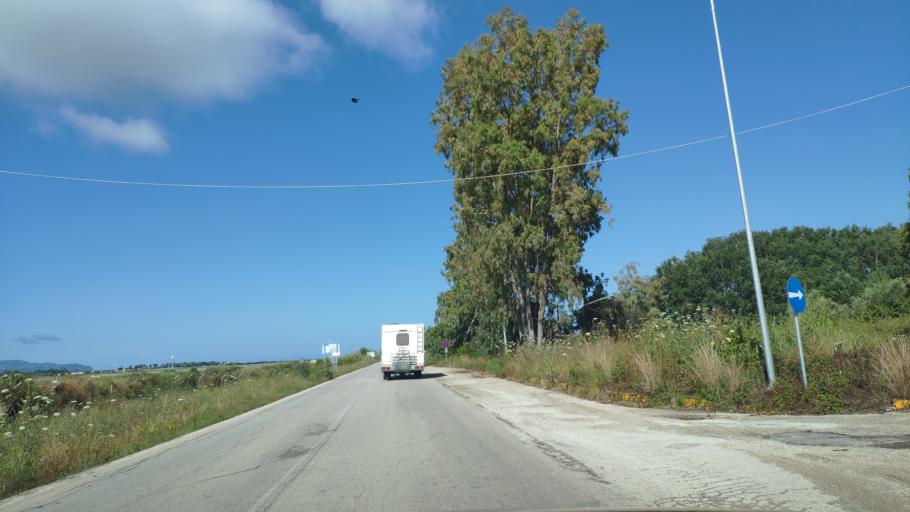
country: GR
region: Epirus
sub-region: Nomos Prevezis
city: Preveza
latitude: 38.9312
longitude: 20.7781
